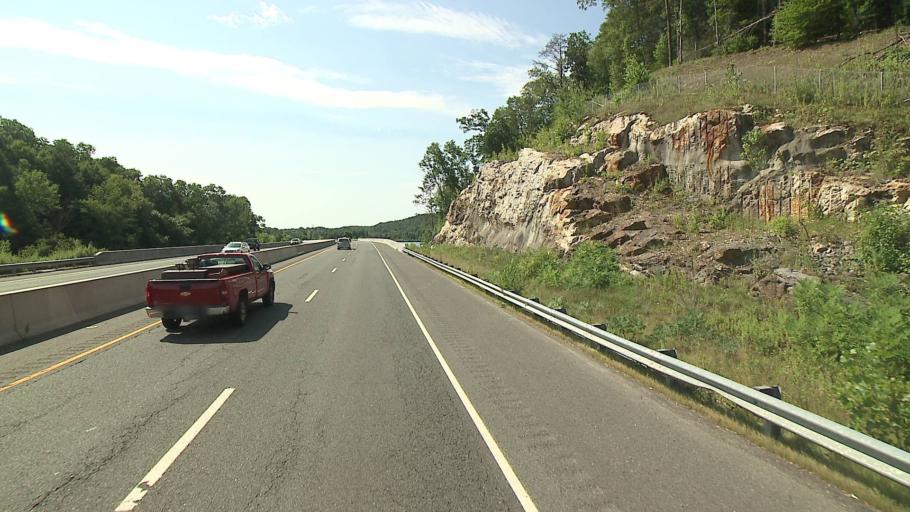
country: US
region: Connecticut
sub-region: Litchfield County
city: New Milford
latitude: 41.4875
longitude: -73.4187
